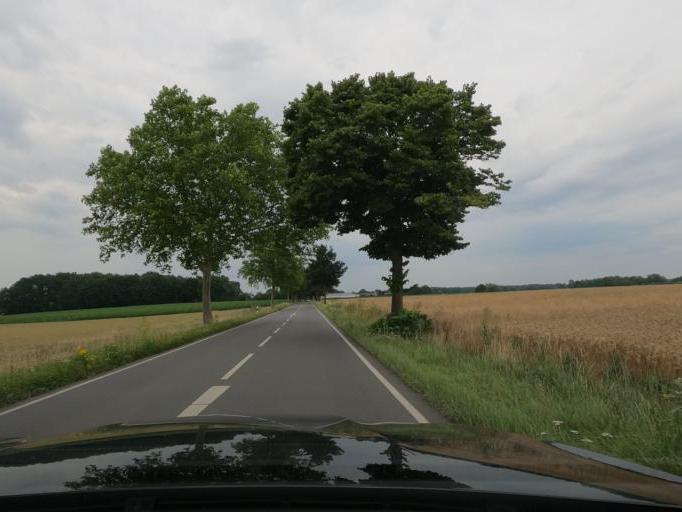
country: DE
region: Lower Saxony
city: Neustadt am Rubenberge
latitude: 52.5429
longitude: 9.5033
